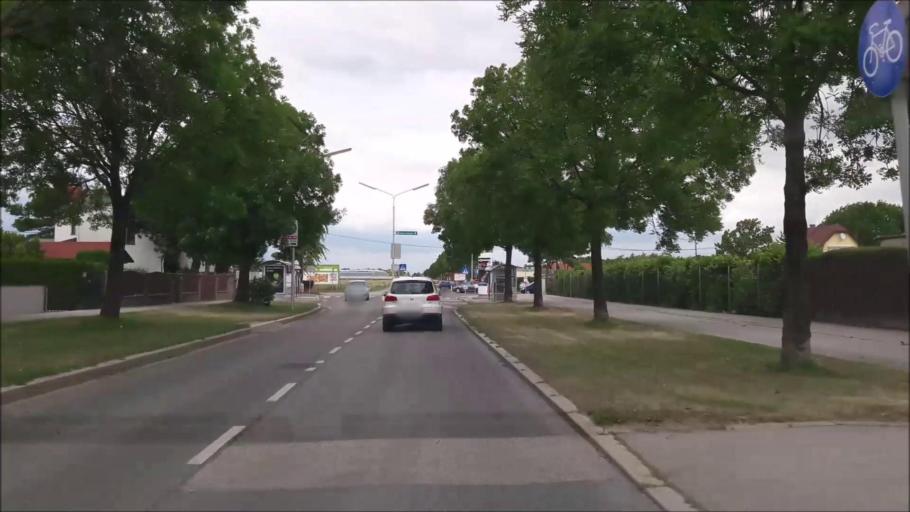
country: AT
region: Lower Austria
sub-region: Politischer Bezirk Wien-Umgebung
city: Gerasdorf bei Wien
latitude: 48.2266
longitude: 16.4844
